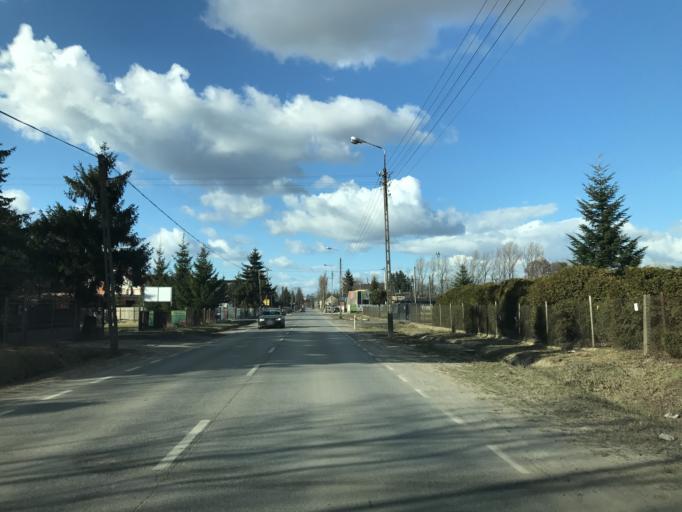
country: PL
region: Masovian Voivodeship
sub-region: Powiat wolominski
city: Radzymin
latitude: 52.4091
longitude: 21.1914
